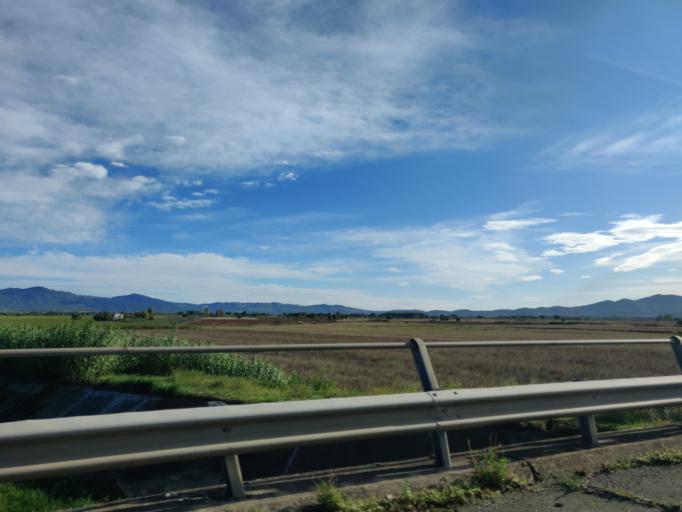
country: IT
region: Tuscany
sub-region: Provincia di Grosseto
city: Braccagni
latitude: 42.9047
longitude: 11.0377
